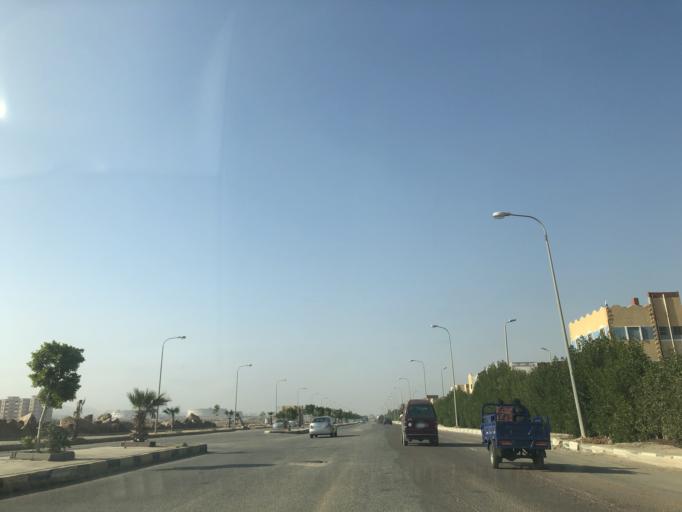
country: EG
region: Al Jizah
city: Madinat Sittah Uktubar
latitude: 29.9282
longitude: 31.0500
